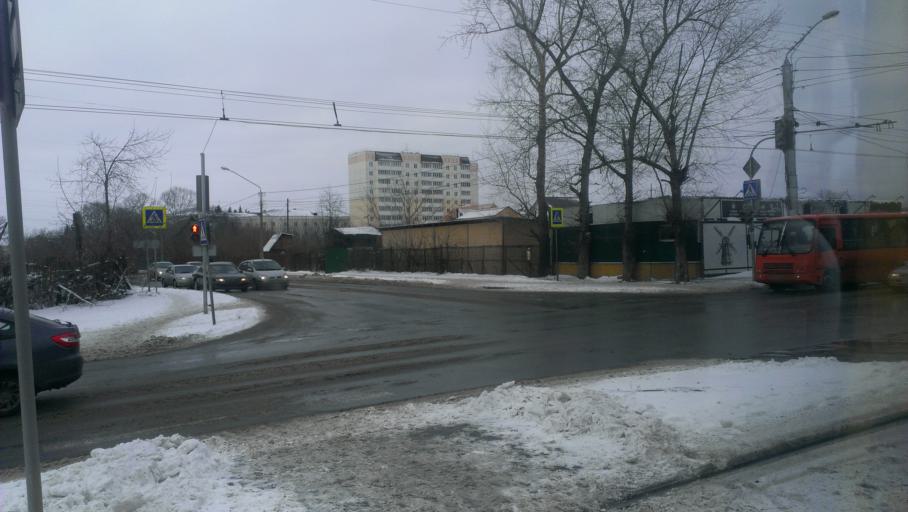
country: RU
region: Altai Krai
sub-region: Gorod Barnaulskiy
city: Barnaul
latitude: 53.3792
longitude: 83.7131
